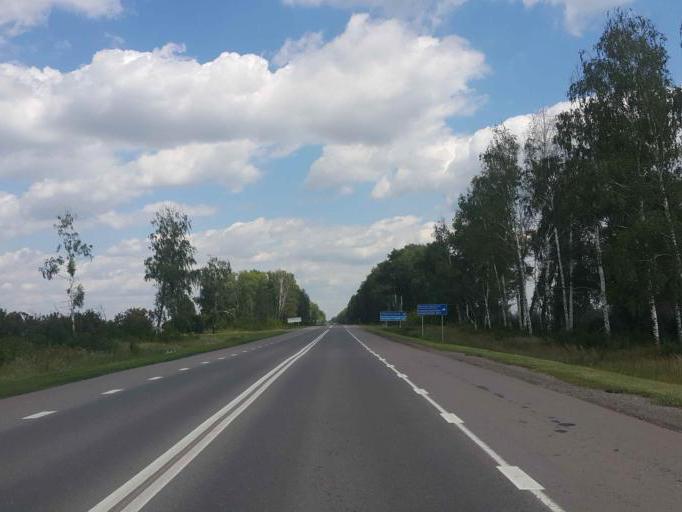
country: RU
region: Tambov
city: Goreloye
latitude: 53.0552
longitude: 41.4825
